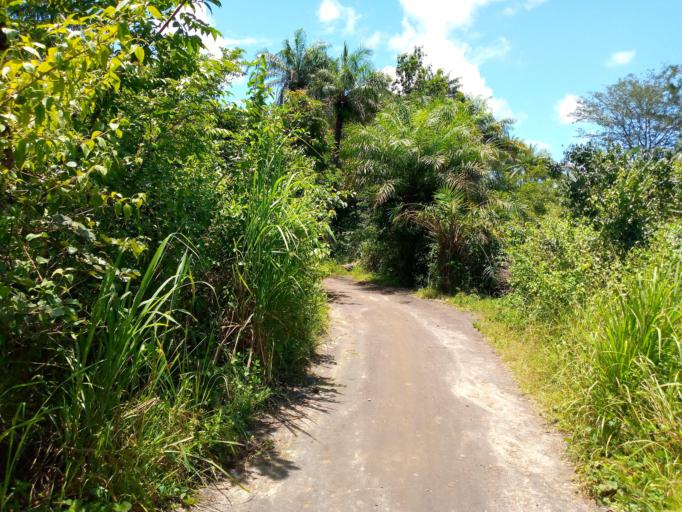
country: SL
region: Northern Province
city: Binkolo
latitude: 9.0589
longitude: -12.1518
